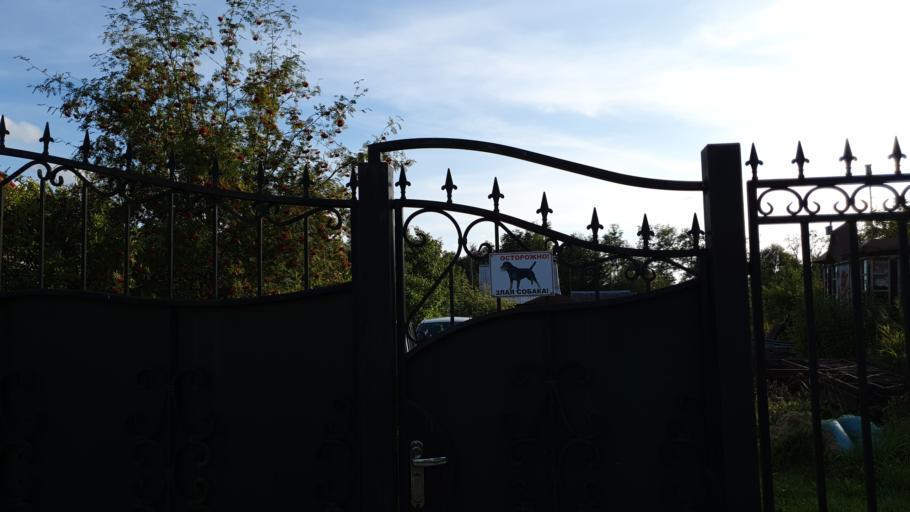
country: RU
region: Leningrad
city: Ivangorod
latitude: 59.4228
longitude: 28.3355
